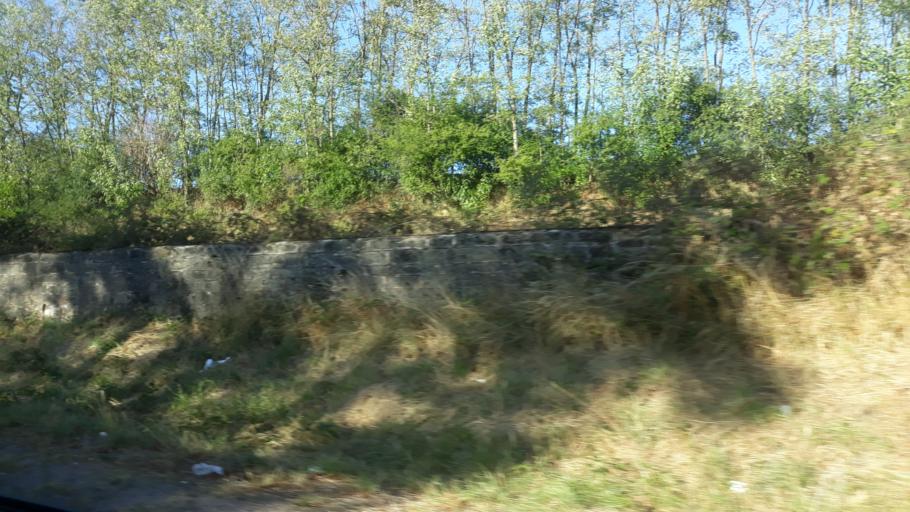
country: FR
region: Bourgogne
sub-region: Departement de Saone-et-Loire
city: Torcy
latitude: 46.7724
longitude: 4.4490
